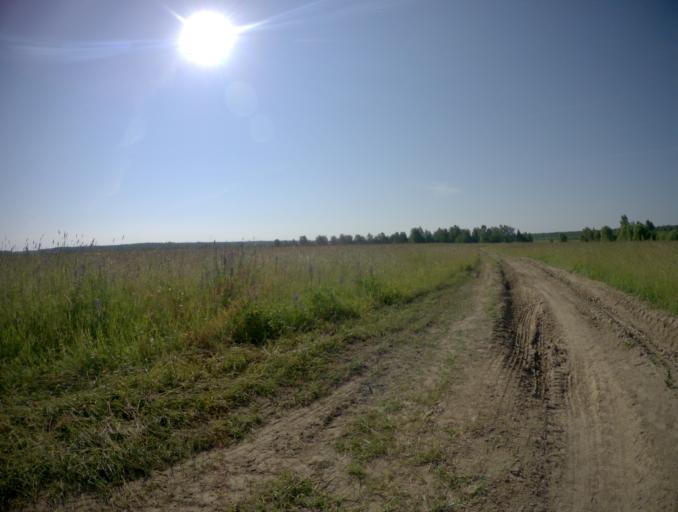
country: RU
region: Vladimir
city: Novovyazniki
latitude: 56.1934
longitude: 42.1920
